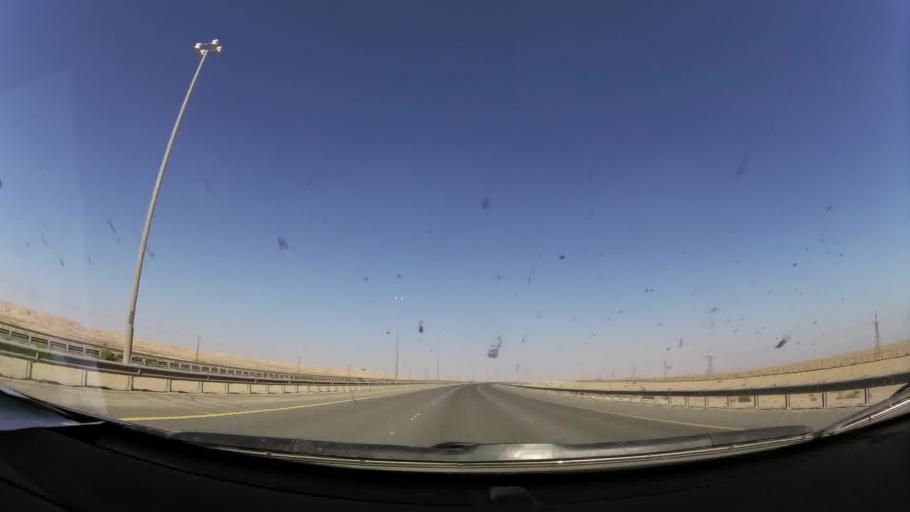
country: KW
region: Al Asimah
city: Kuwait City
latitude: 29.5140
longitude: 47.8045
